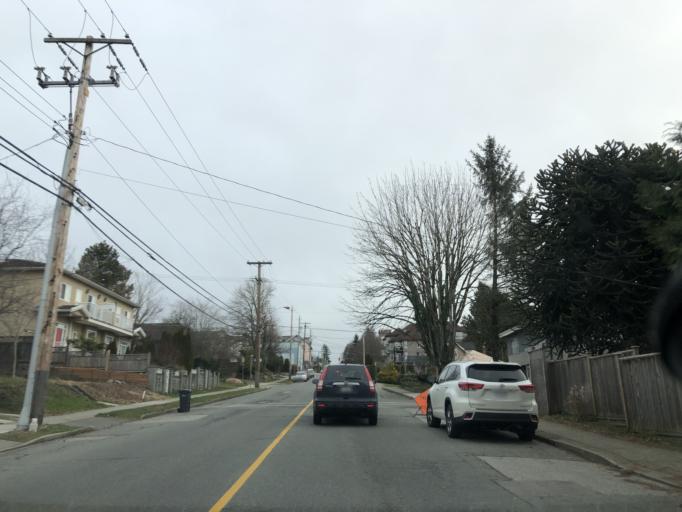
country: CA
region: British Columbia
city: New Westminster
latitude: 49.2064
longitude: -122.9329
